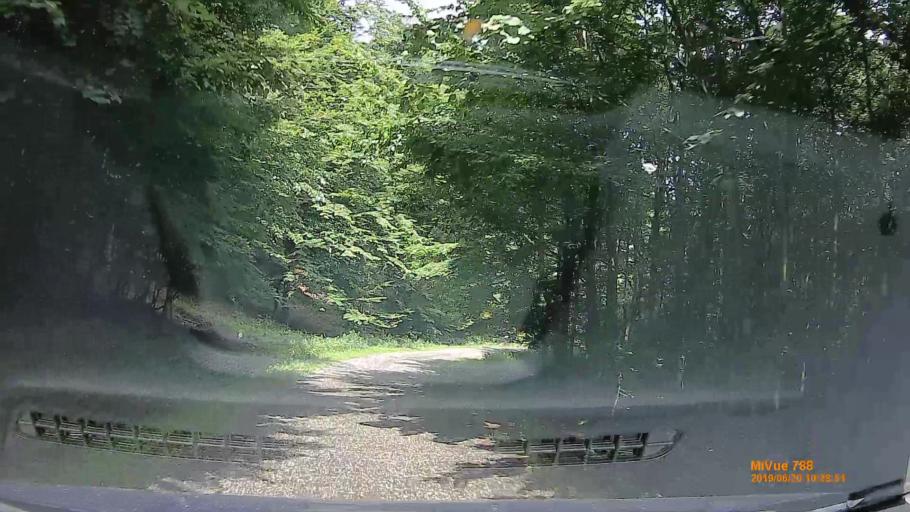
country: HU
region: Baranya
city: Mecseknadasd
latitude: 46.2081
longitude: 18.4921
